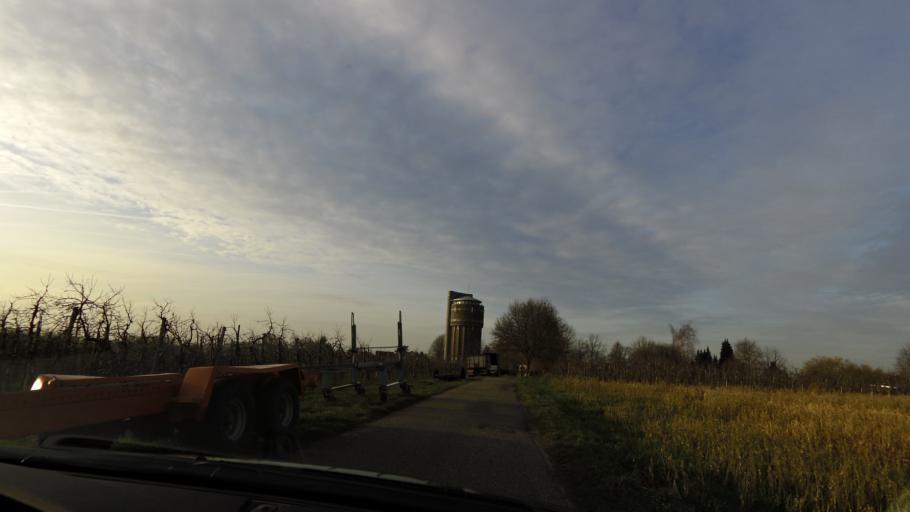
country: NL
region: Limburg
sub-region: Valkenburg aan de Geul
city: Broekhem
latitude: 50.8998
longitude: 5.8256
